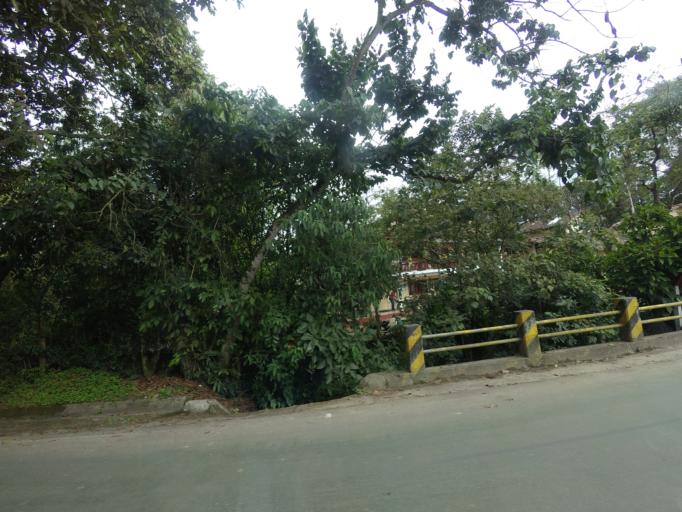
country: CO
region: Huila
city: San Agustin
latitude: 1.8873
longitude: -76.2800
